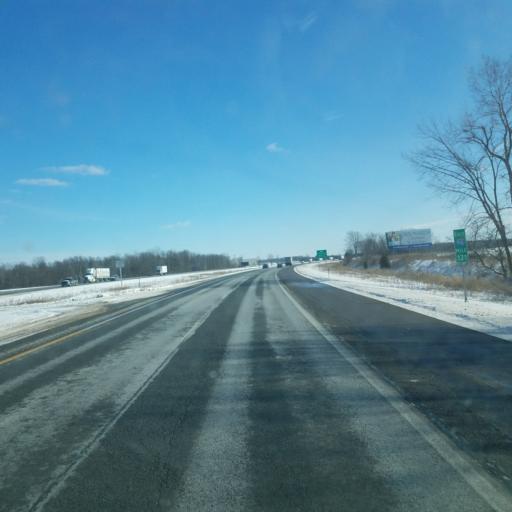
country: US
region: Michigan
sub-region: Ingham County
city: Webberville
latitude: 42.6654
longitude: -84.2135
